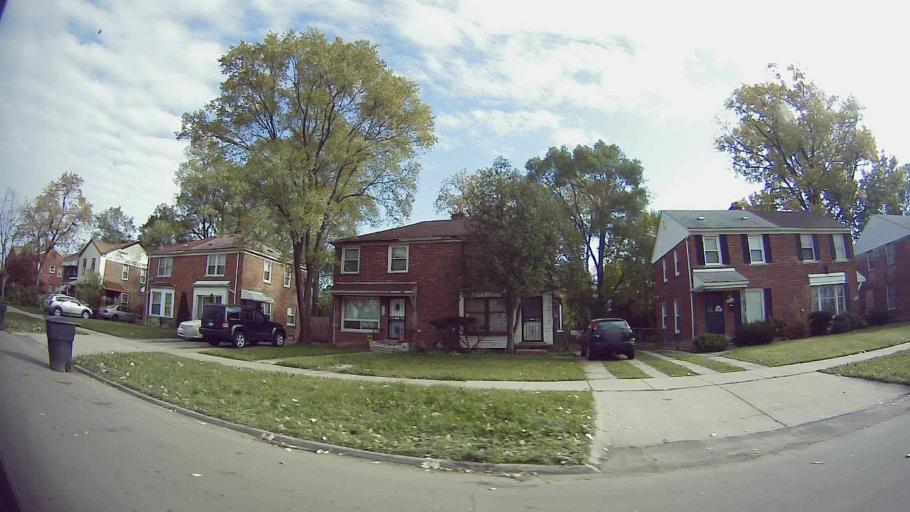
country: US
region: Michigan
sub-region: Oakland County
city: Oak Park
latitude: 42.4412
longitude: -83.1808
